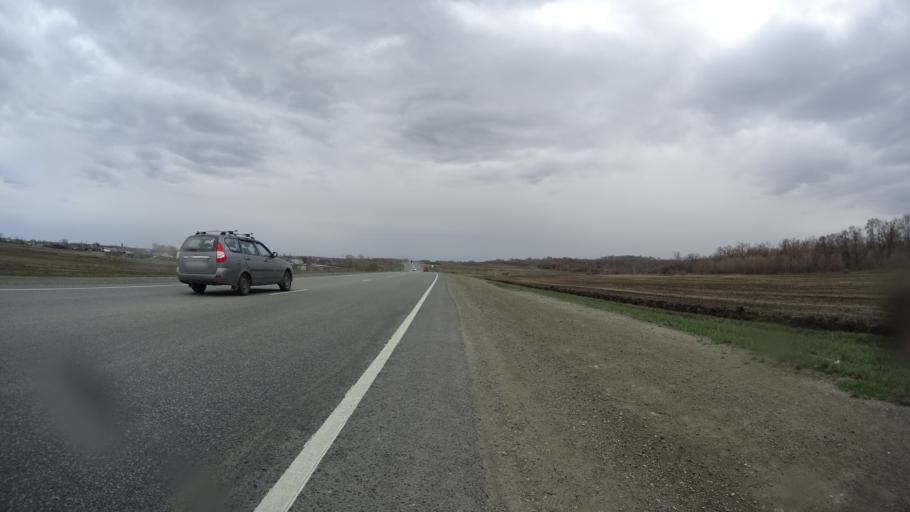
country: RU
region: Chelyabinsk
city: Krasnogorskiy
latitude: 54.6783
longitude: 61.2473
